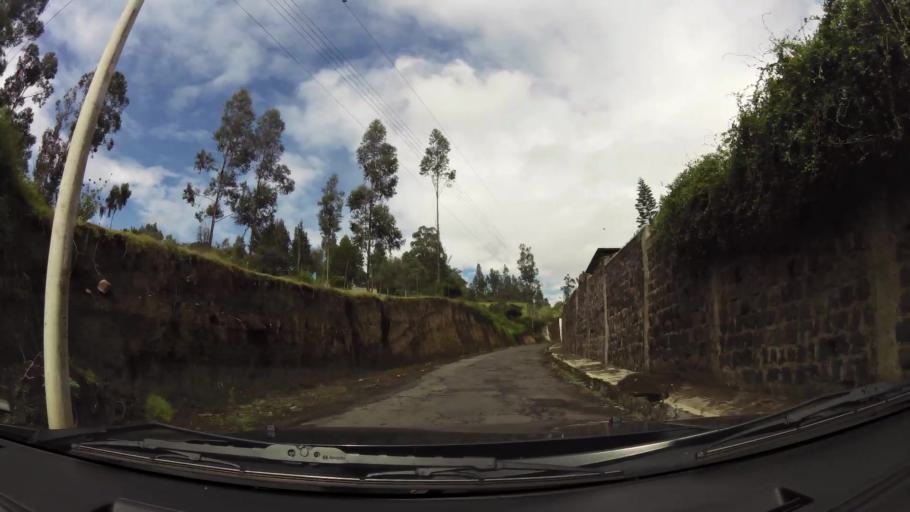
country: EC
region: Pichincha
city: Sangolqui
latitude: -0.3044
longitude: -78.4280
